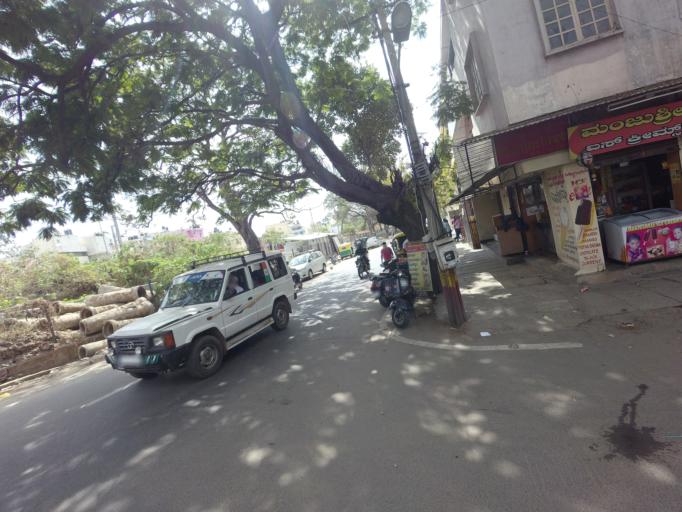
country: IN
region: Karnataka
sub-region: Bangalore Urban
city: Bangalore
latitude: 12.9573
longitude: 77.5382
